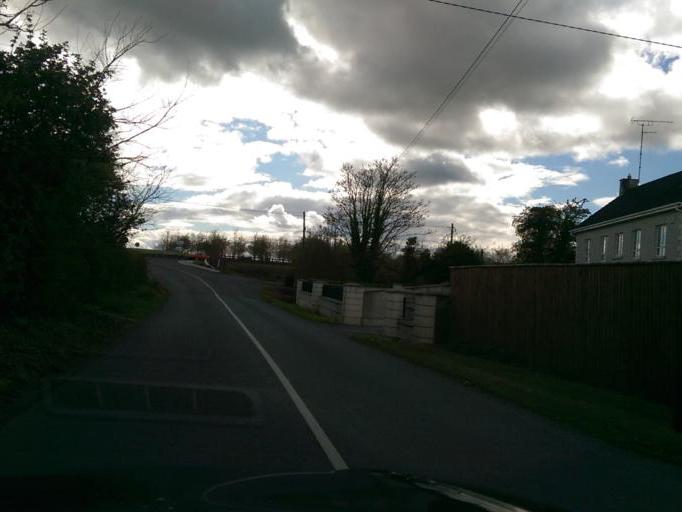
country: IE
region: Leinster
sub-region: An Mhi
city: Dunshaughlin
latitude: 53.5220
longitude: -6.6492
